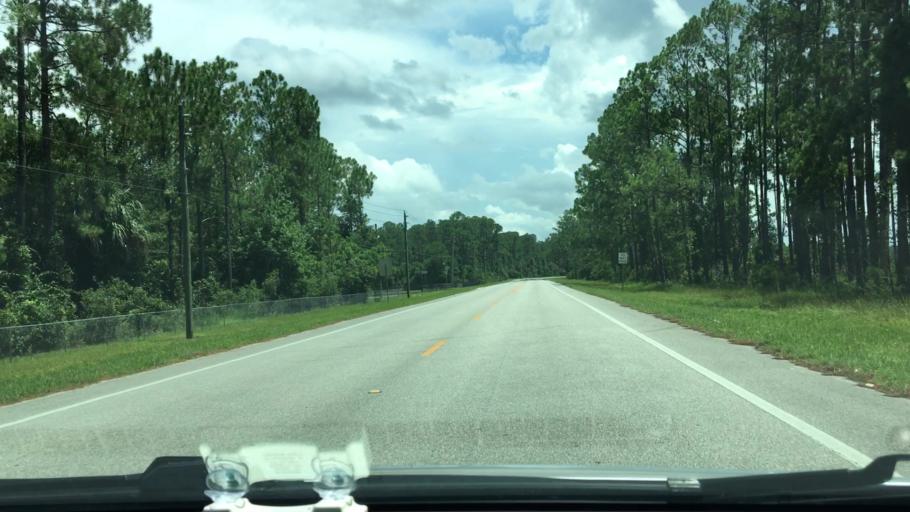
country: US
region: Florida
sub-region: Volusia County
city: Samsula-Spruce Creek
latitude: 29.0312
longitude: -81.0666
